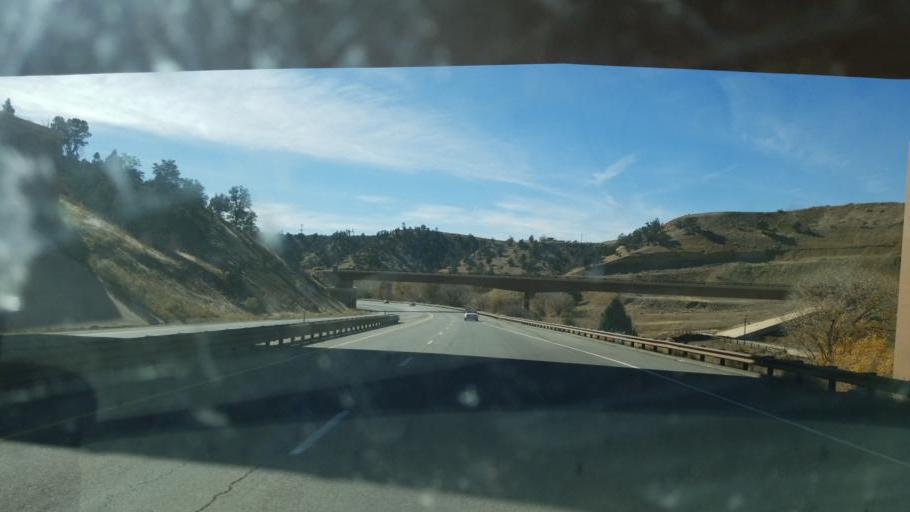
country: US
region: Colorado
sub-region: La Plata County
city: Durango
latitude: 37.2277
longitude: -107.8390
